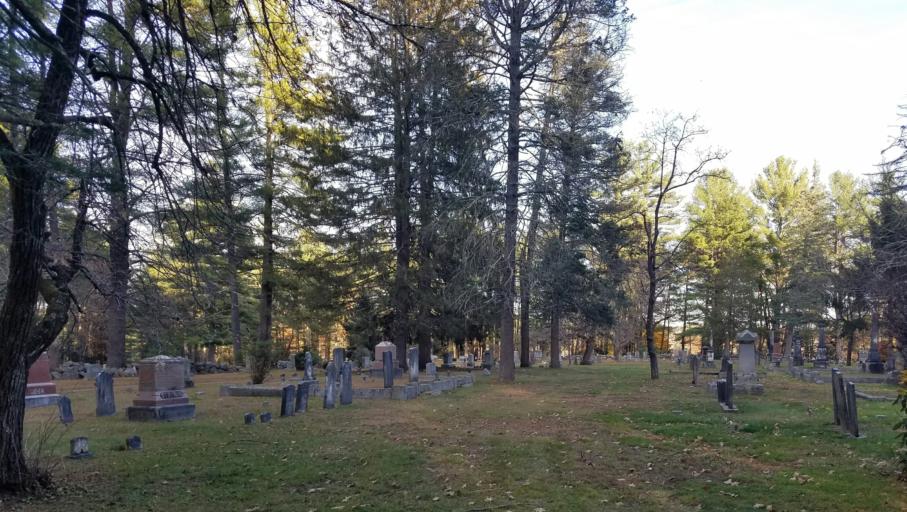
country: US
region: New Hampshire
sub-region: Merrimack County
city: Henniker
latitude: 43.1806
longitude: -71.8147
